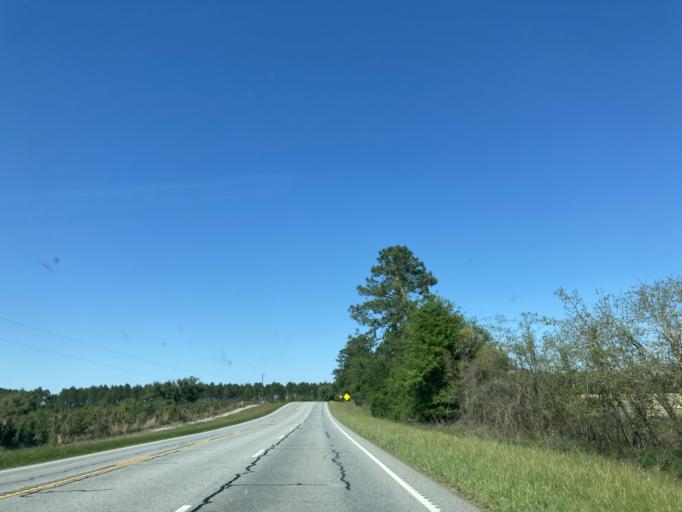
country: US
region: Georgia
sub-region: Baker County
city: Newton
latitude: 31.2466
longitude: -84.4298
